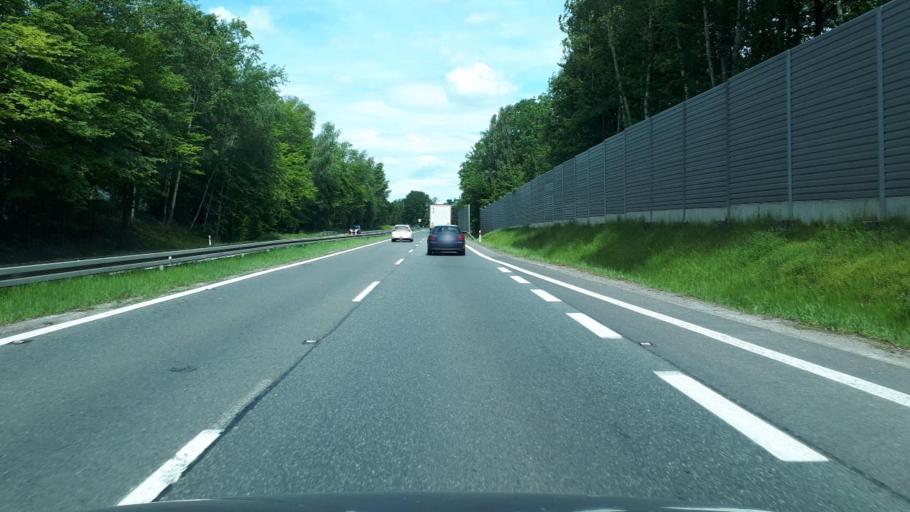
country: PL
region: Silesian Voivodeship
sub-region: Powiat bielski
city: Mazancowice
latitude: 49.8753
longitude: 19.0006
